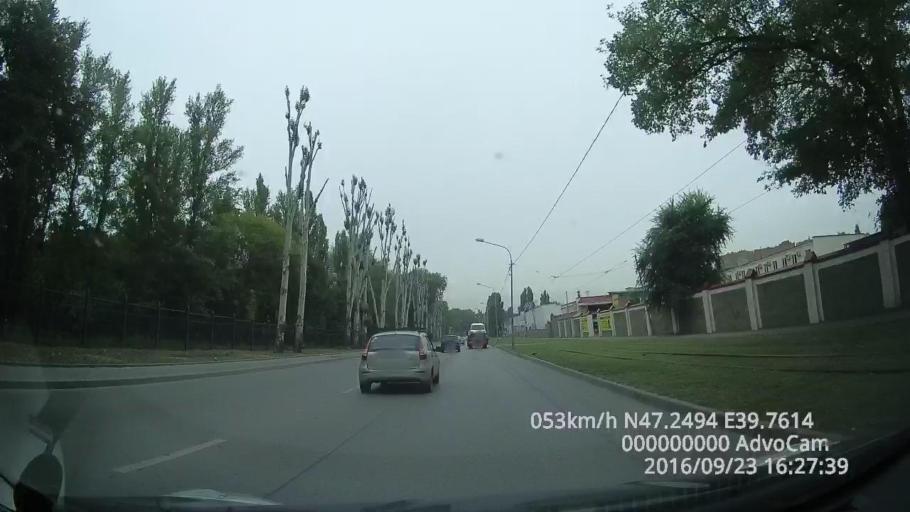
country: RU
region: Rostov
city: Imeni Chkalova
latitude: 47.2493
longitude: 39.7613
